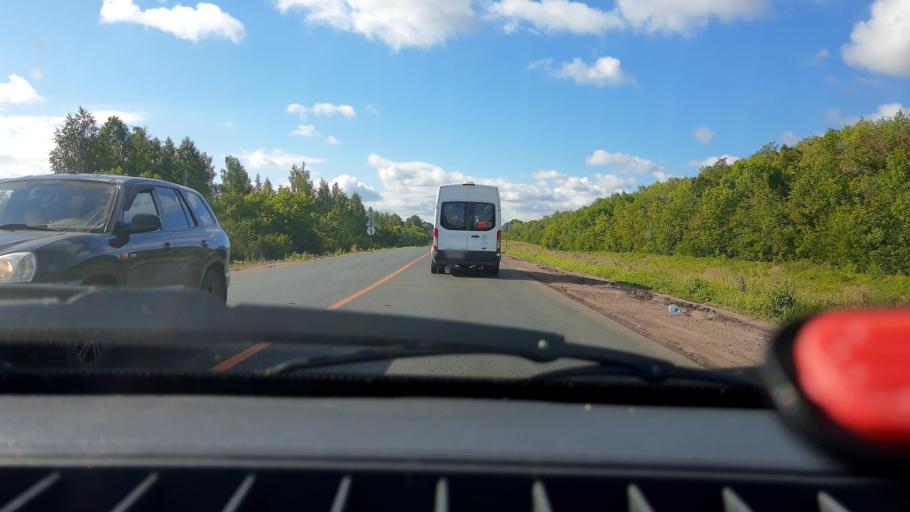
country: RU
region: Bashkortostan
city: Zirgan
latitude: 53.1676
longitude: 55.9042
